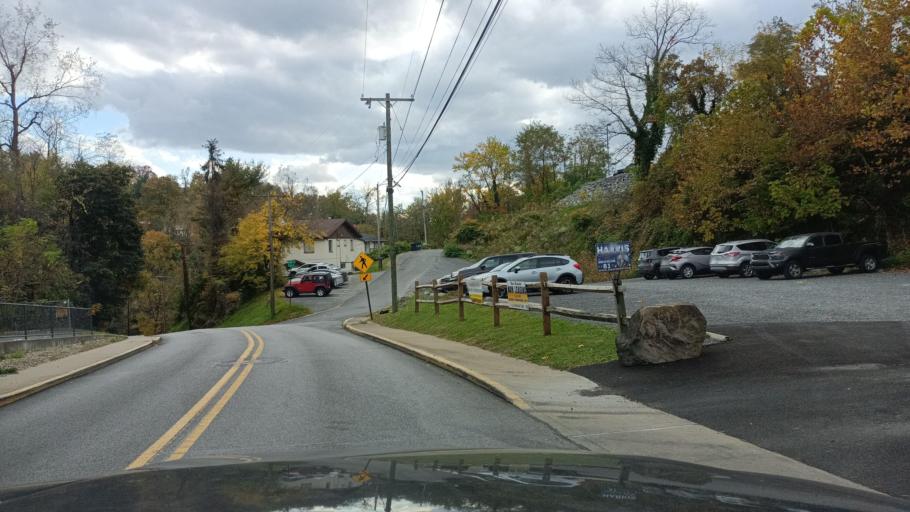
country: US
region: West Virginia
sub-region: Monongalia County
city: Morgantown
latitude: 39.6407
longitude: -79.9494
